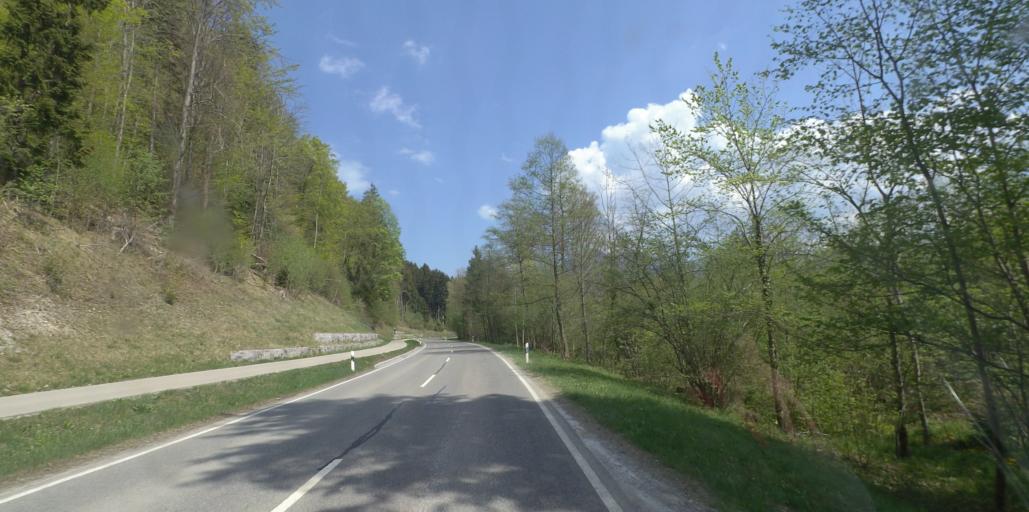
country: DE
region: Bavaria
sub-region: Upper Bavaria
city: Schleching
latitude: 47.7362
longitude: 12.4213
